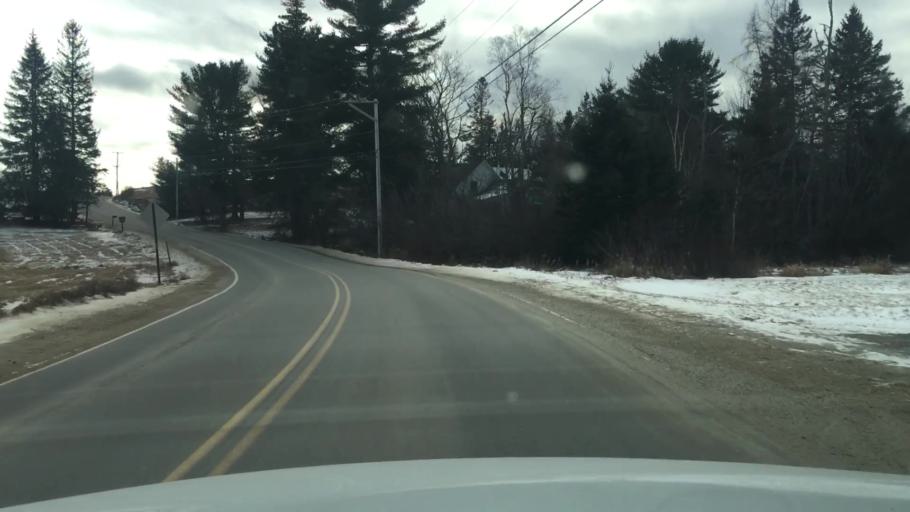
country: US
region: Maine
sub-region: Washington County
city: Jonesport
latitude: 44.6247
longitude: -67.6015
